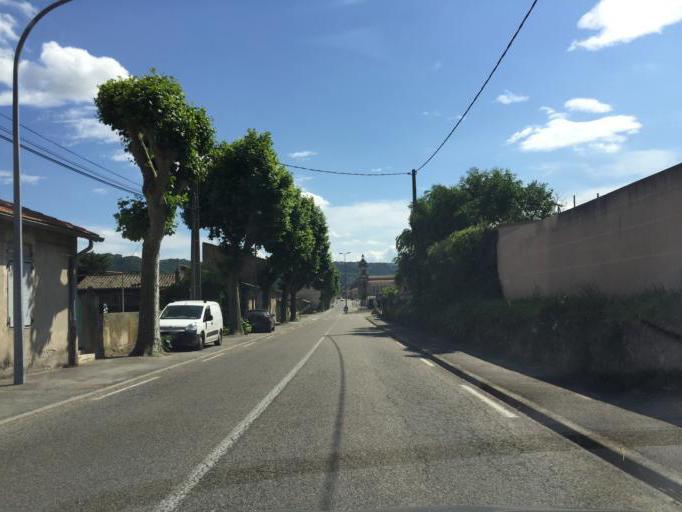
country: FR
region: Rhone-Alpes
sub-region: Departement de l'Ardeche
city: Saint-Jean-de-Muzols
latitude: 45.0861
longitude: 4.8172
